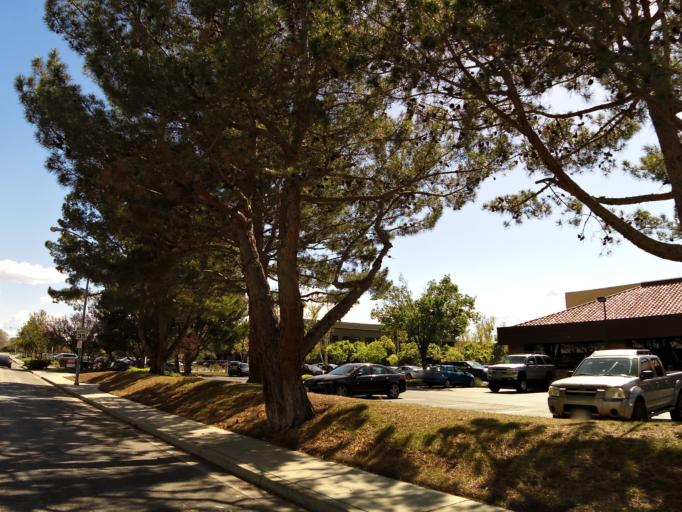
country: US
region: California
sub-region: Santa Clara County
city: Milpitas
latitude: 37.4815
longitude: -121.9414
